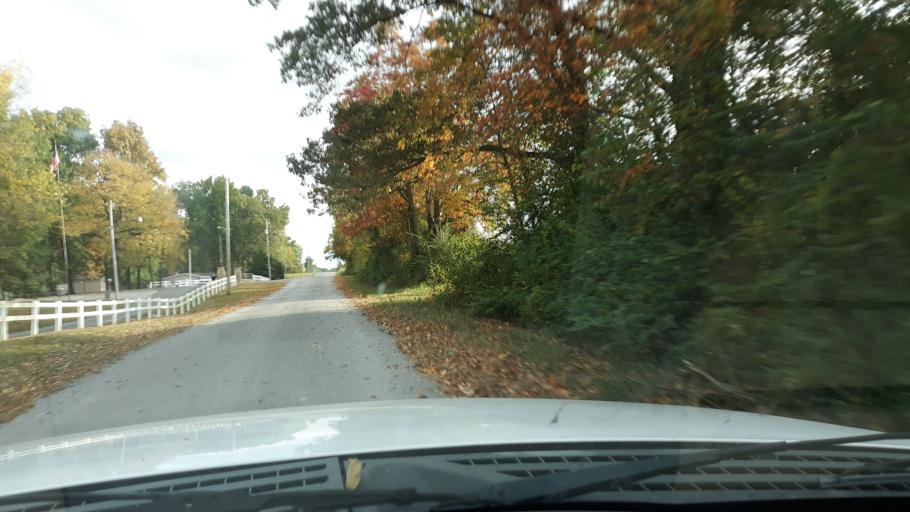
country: US
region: Illinois
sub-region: Saline County
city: Eldorado
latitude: 37.8288
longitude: -88.5025
